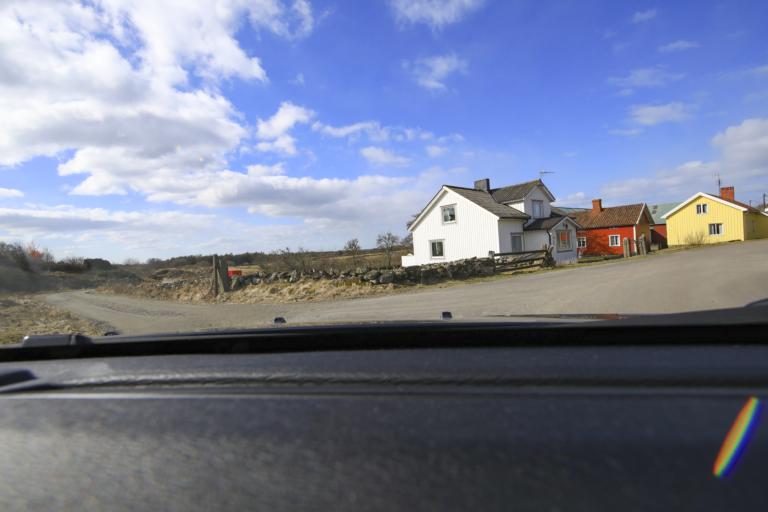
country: SE
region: Halland
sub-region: Kungsbacka Kommun
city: Frillesas
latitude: 57.2256
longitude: 12.1389
